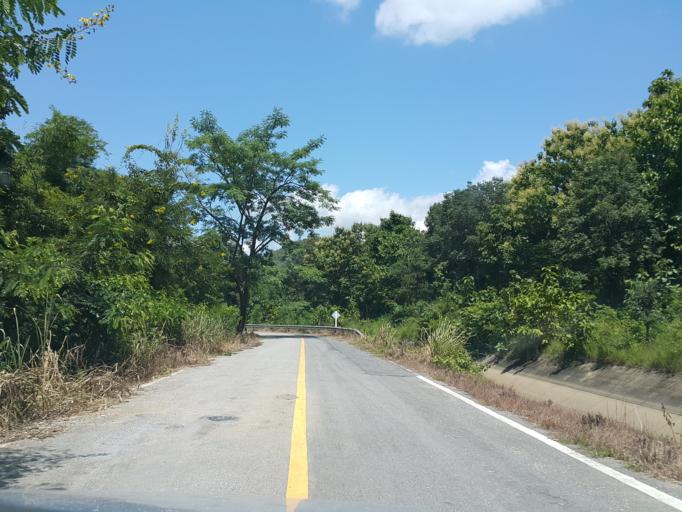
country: TH
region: Lamphun
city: Ban Thi
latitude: 18.6858
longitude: 99.1792
